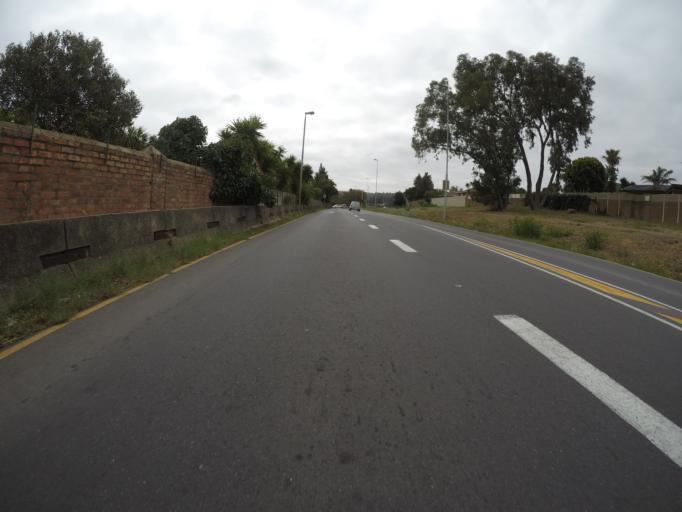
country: ZA
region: Western Cape
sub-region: City of Cape Town
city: Kraaifontein
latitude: -33.8509
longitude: 18.6299
